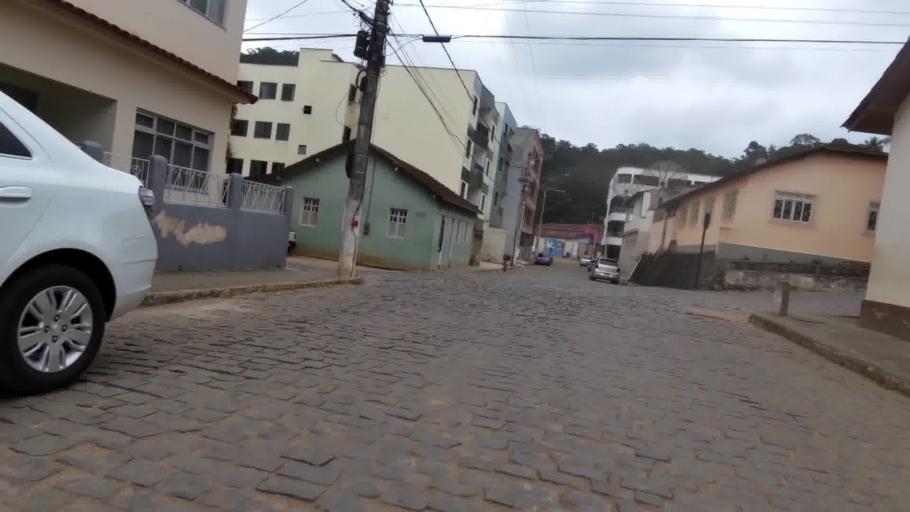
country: BR
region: Espirito Santo
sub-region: Alfredo Chaves
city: Alfredo Chaves
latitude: -20.6355
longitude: -40.7519
